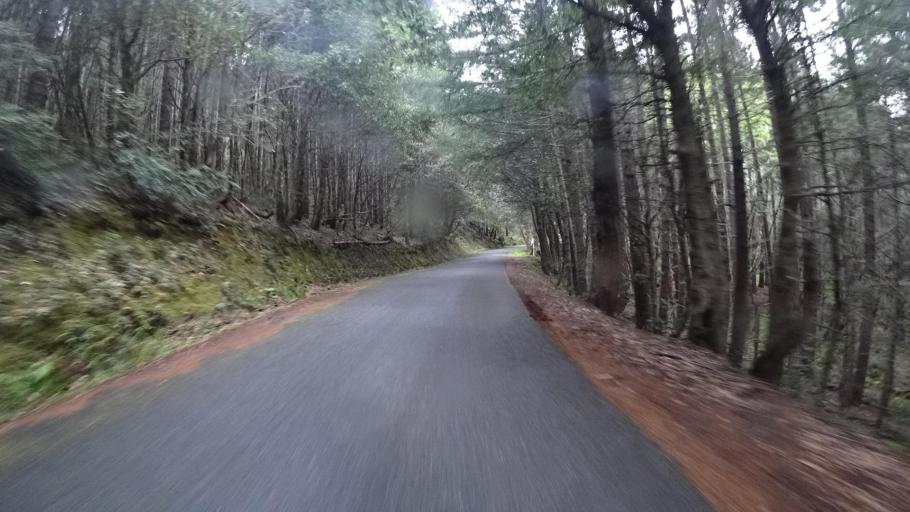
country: US
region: California
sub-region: Humboldt County
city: Willow Creek
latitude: 41.2032
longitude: -123.7737
